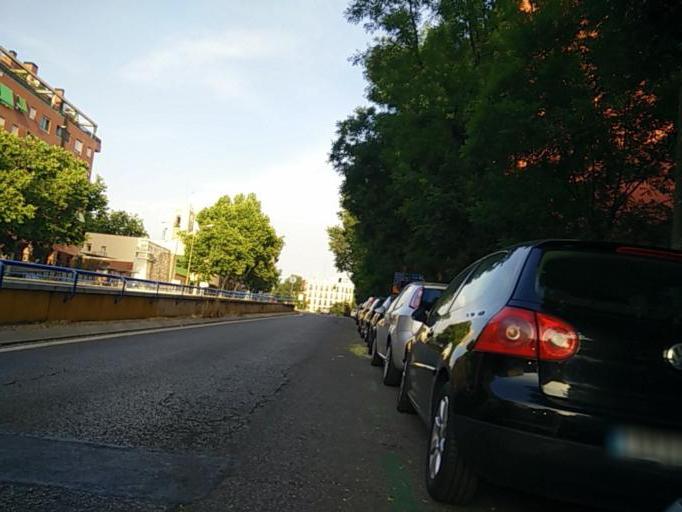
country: ES
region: Madrid
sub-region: Provincia de Madrid
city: Madrid
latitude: 40.4073
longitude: -3.7136
